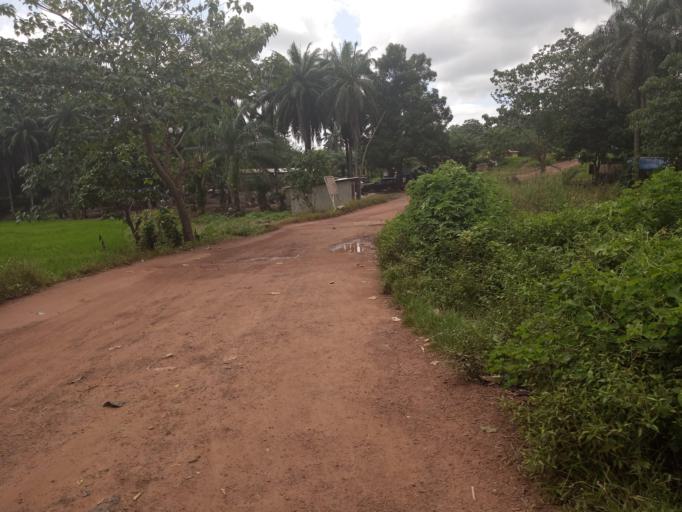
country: SL
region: Northern Province
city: Kamakwie
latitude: 9.4969
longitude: -12.2461
